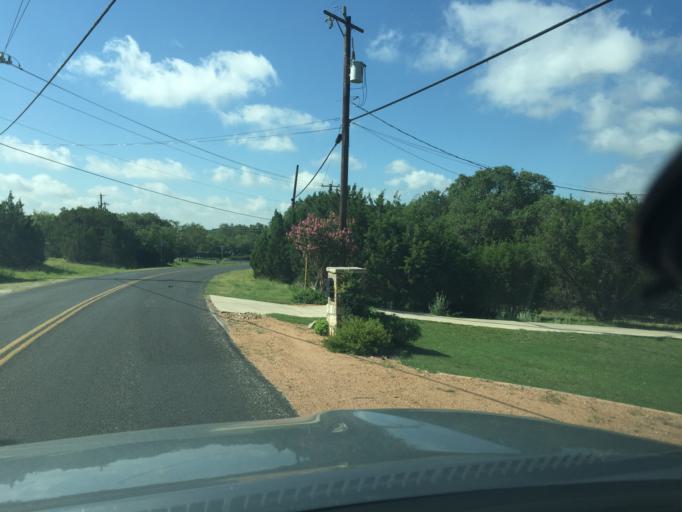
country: US
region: Texas
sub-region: Bexar County
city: Timberwood Park
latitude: 29.7026
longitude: -98.4901
